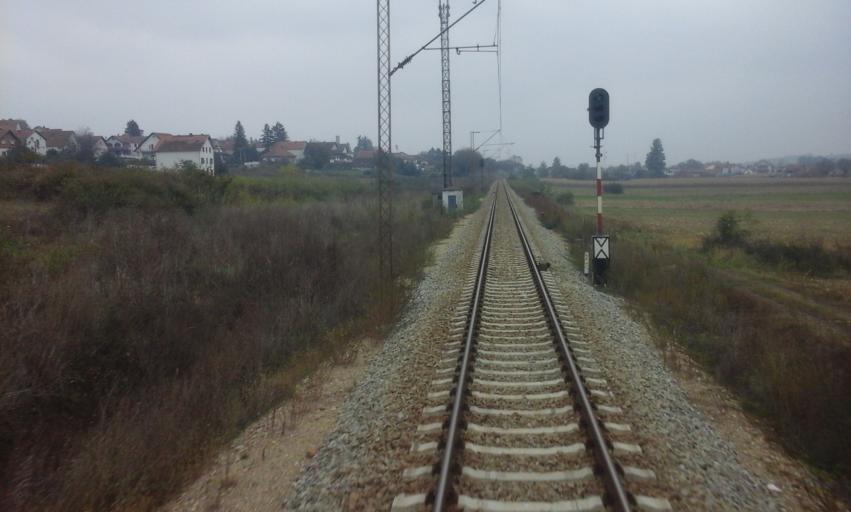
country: RS
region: Central Serbia
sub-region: Belgrade
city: Mladenovac
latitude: 44.4538
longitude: 20.6765
